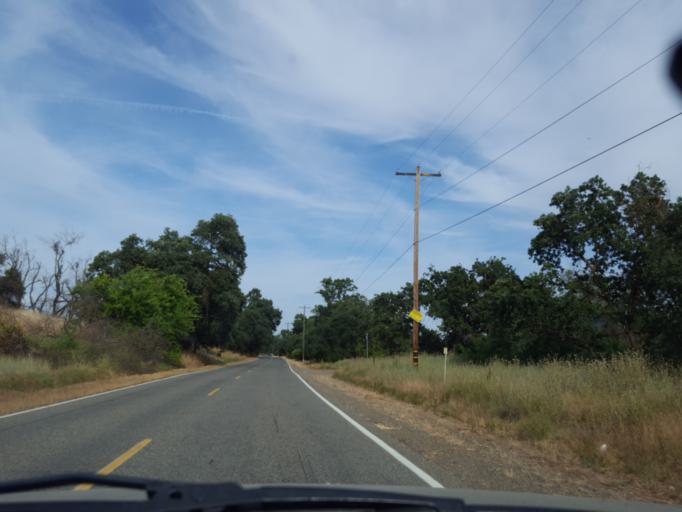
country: US
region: California
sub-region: Merced County
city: Planada
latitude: 37.5184
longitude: -120.3799
